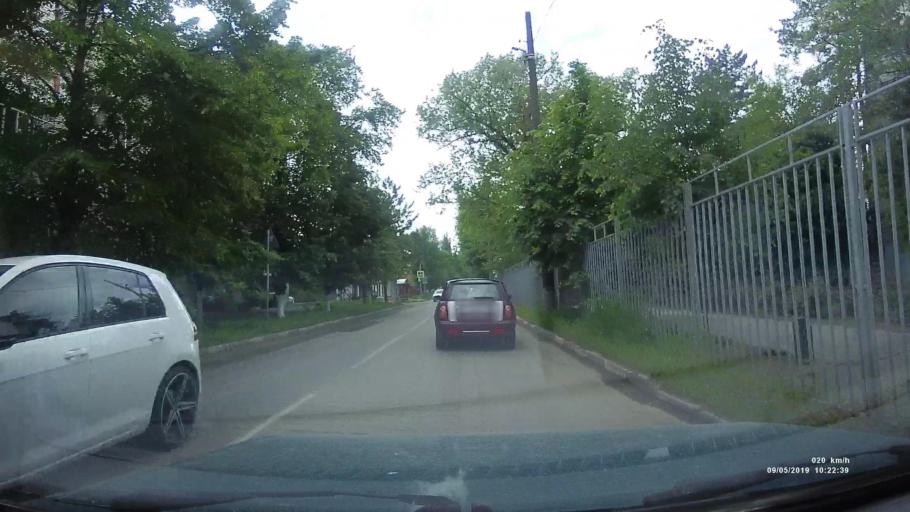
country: RU
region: Rostov
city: Azov
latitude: 47.1046
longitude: 39.4224
